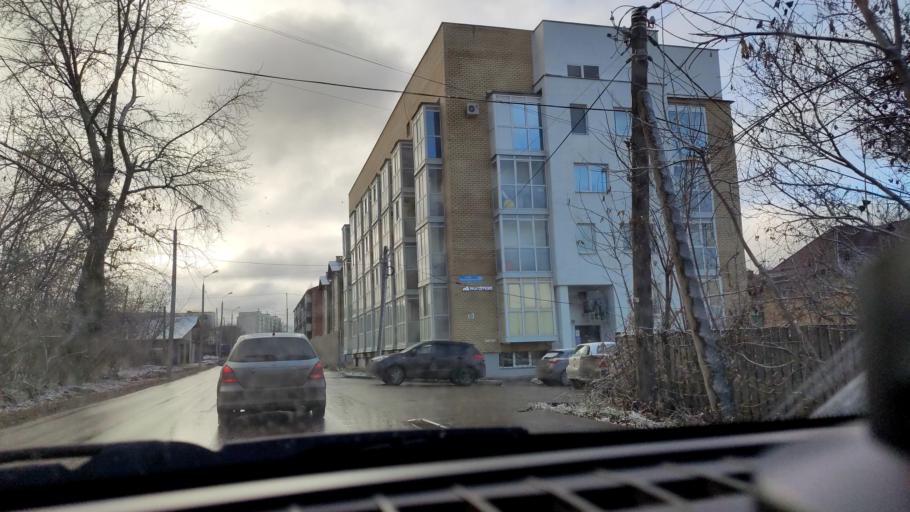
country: RU
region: Perm
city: Perm
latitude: 57.9744
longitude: 56.1942
